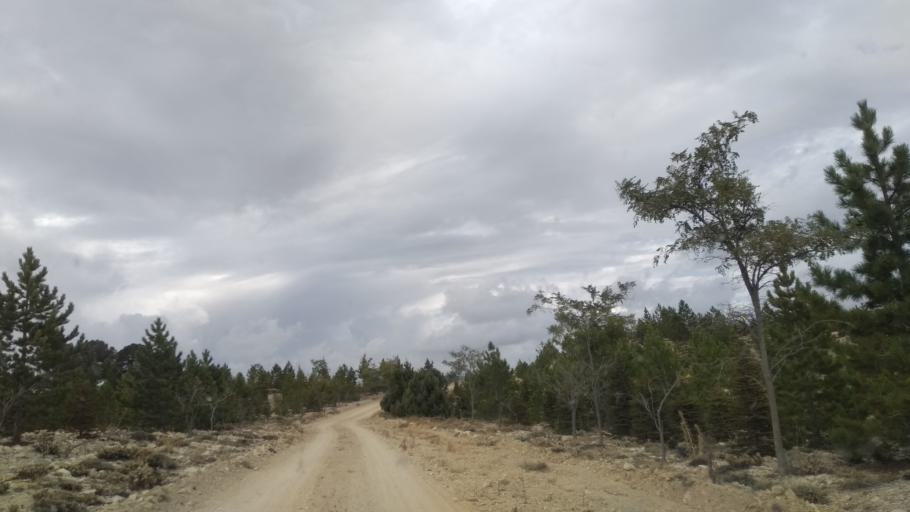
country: TR
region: Mersin
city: Sarikavak
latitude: 36.5724
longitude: 33.7557
